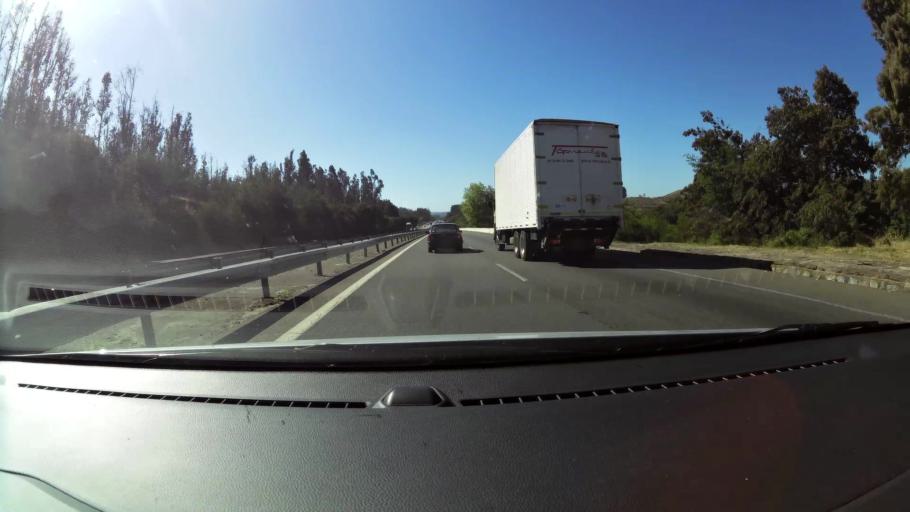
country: CL
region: Valparaiso
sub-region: Provincia de Marga Marga
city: Quilpue
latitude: -33.1992
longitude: -71.4908
